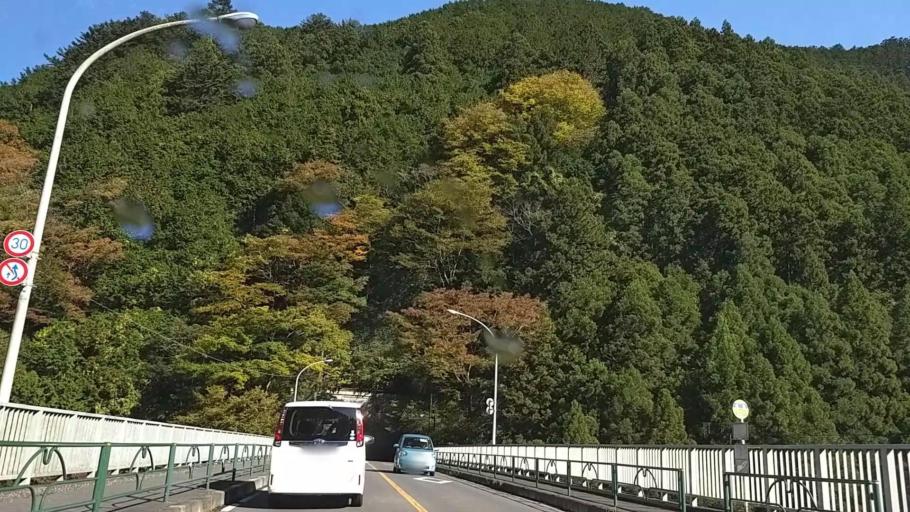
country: JP
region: Tokyo
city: Itsukaichi
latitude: 35.7979
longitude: 139.0783
